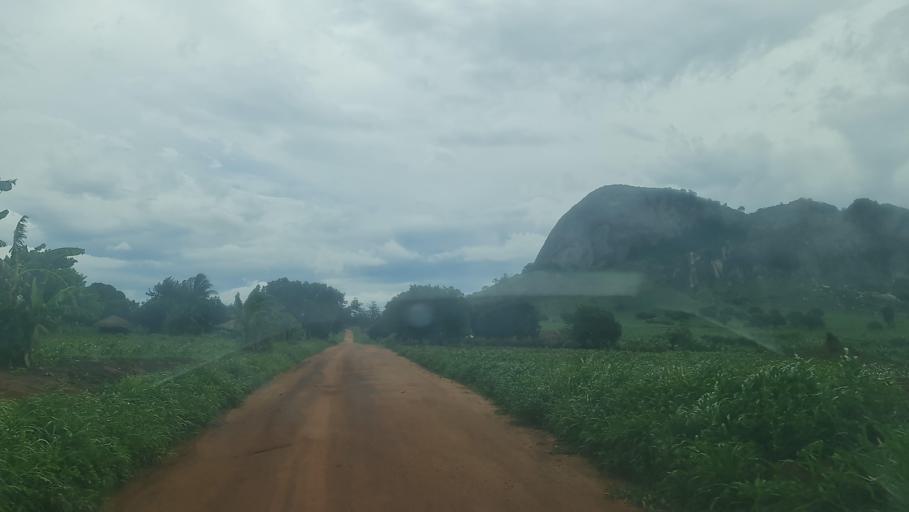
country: MW
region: Southern Region
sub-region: Nsanje District
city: Nsanje
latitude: -17.3980
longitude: 35.5858
